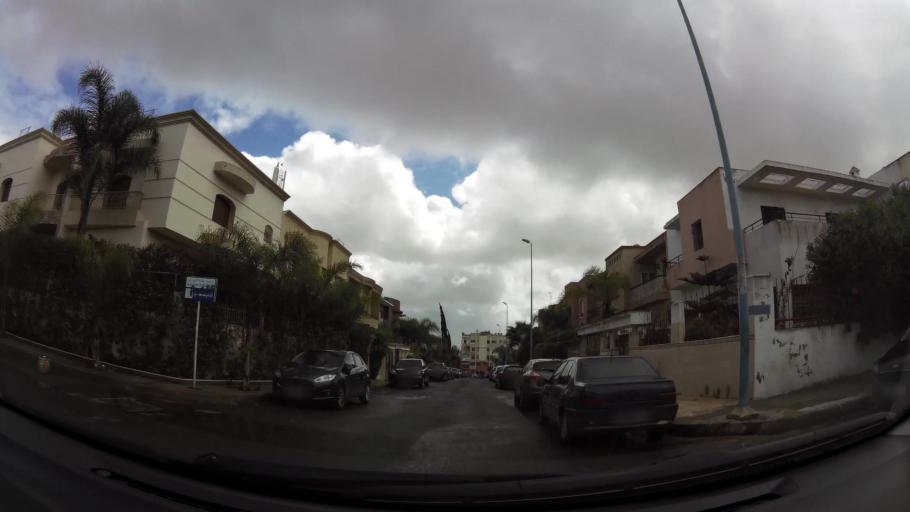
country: MA
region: Grand Casablanca
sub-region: Casablanca
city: Casablanca
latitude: 33.5294
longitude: -7.6447
